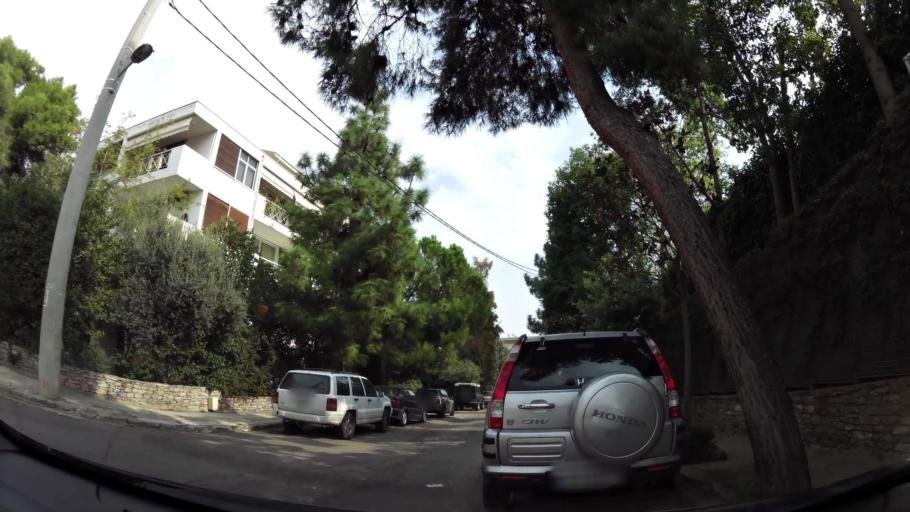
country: GR
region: Attica
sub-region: Nomarchia Athinas
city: Psychiko
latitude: 38.0018
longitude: 23.7700
